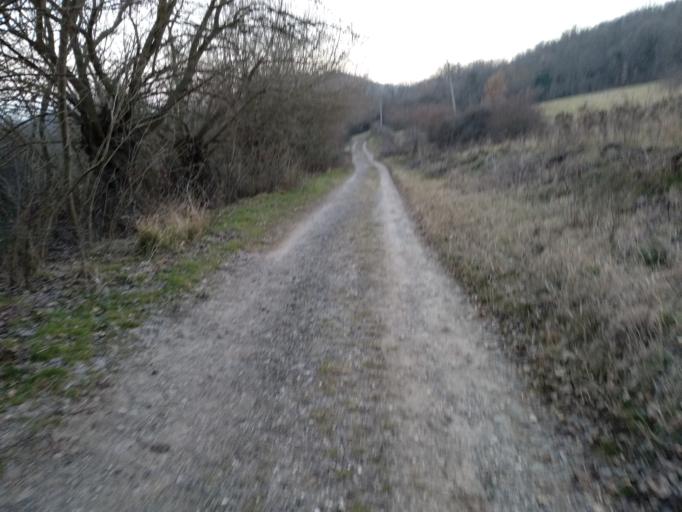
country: IT
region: Veneto
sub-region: Provincia di Padova
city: Battaglia Terme
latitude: 45.3009
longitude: 11.7747
